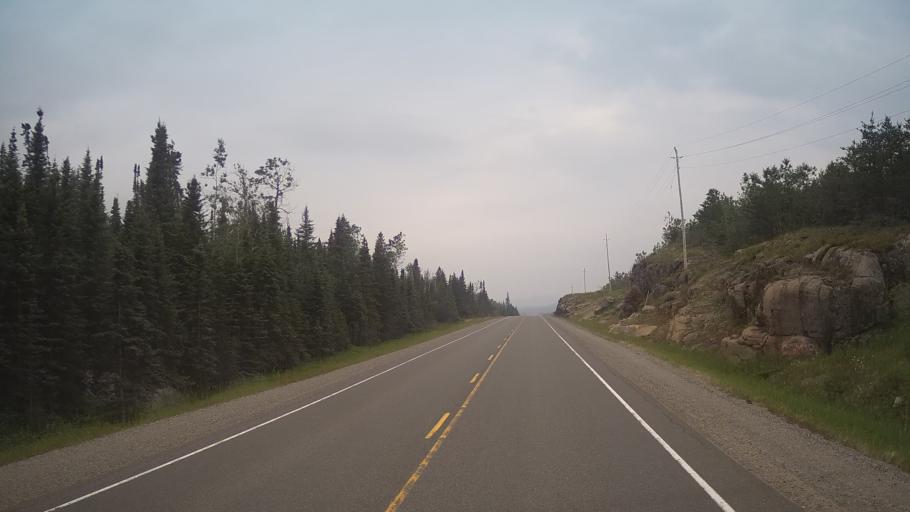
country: CA
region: Ontario
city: Greenstone
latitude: 49.5128
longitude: -88.0383
